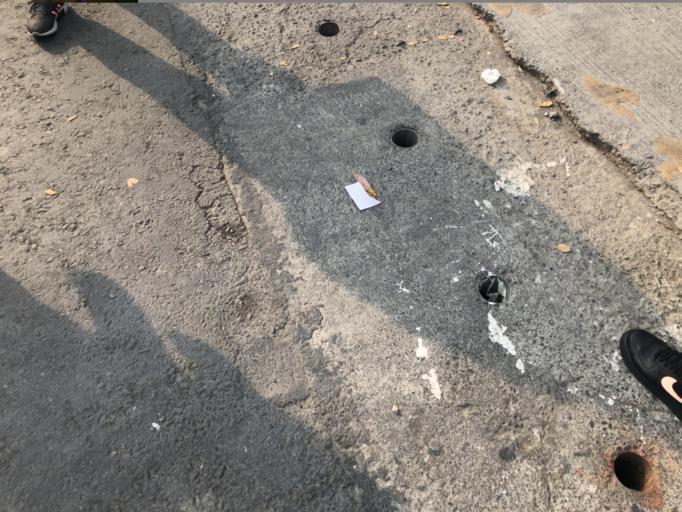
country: TW
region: Taiwan
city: Fengshan
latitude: 22.4682
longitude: 120.4444
